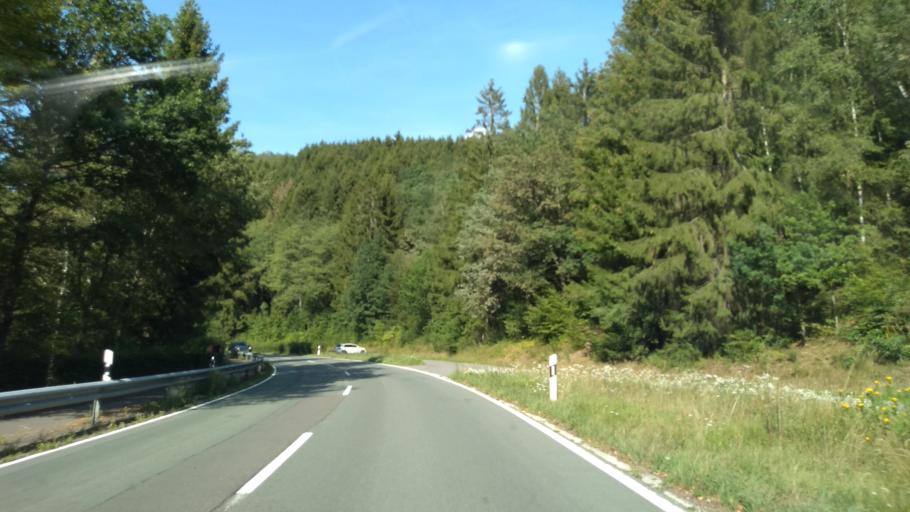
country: DE
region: North Rhine-Westphalia
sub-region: Regierungsbezirk Arnsberg
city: Olpe
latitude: 51.0696
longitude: 7.8635
